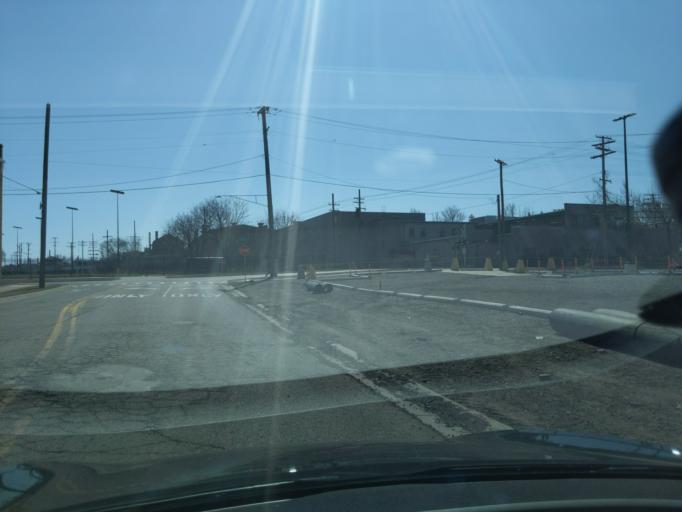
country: US
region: Michigan
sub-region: Washtenaw County
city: Ann Arbor
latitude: 42.2722
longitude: -83.7465
